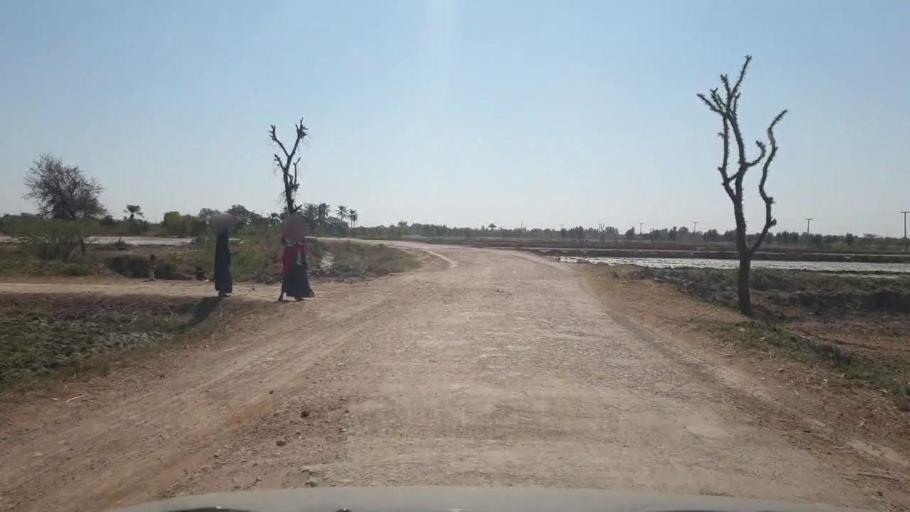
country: PK
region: Sindh
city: Mirwah Gorchani
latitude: 25.3033
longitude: 69.1299
